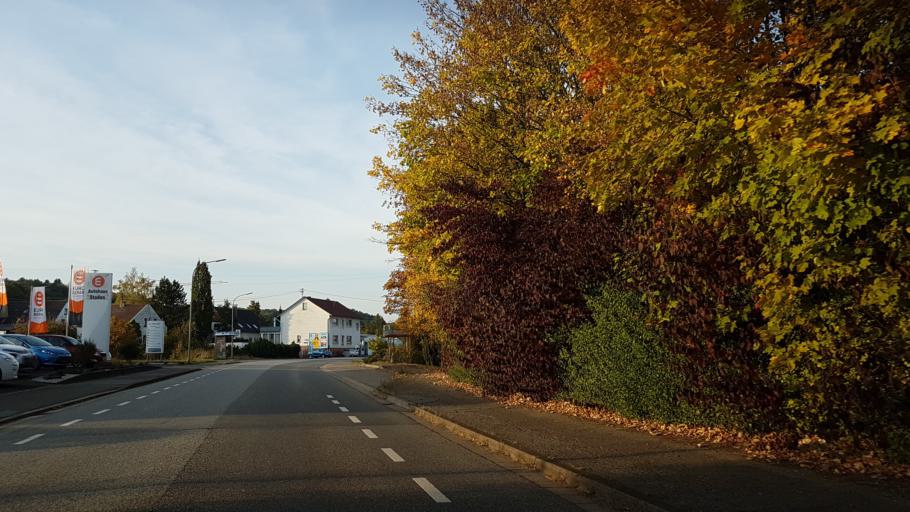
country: DE
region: Saarland
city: Schmelz
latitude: 49.4290
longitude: 6.8469
